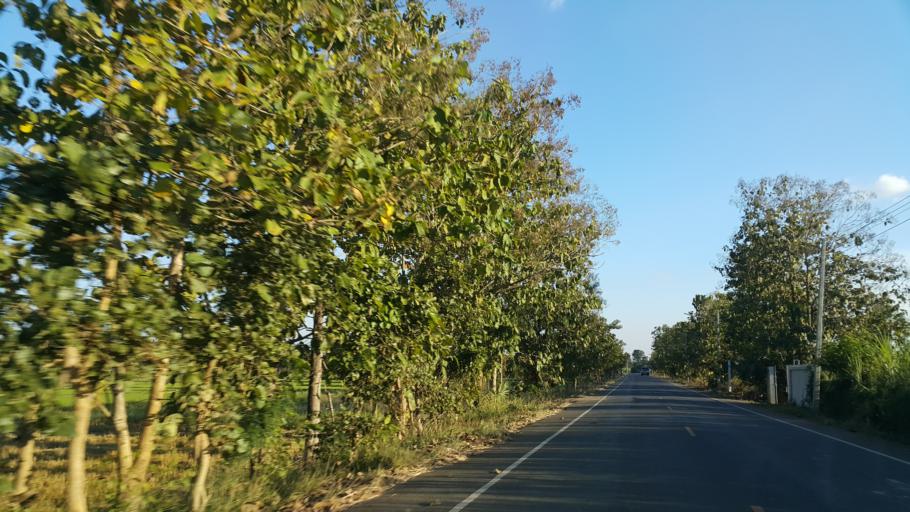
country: TH
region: Sukhothai
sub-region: Amphoe Si Satchanalai
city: Si Satchanalai
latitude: 17.5395
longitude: 99.7982
